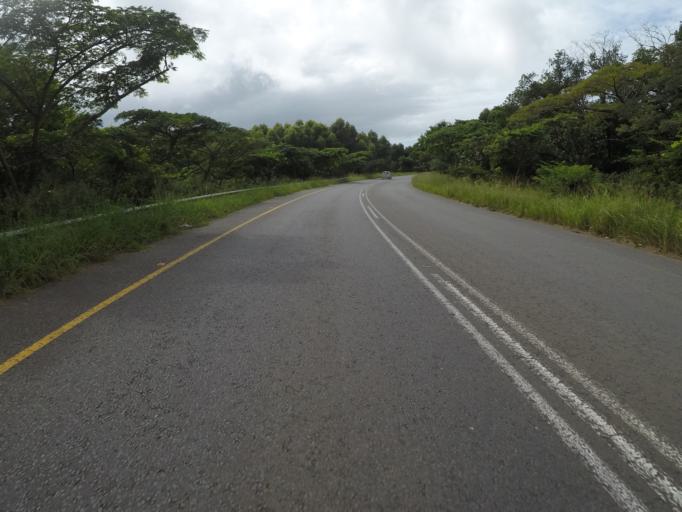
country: ZA
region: KwaZulu-Natal
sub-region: uThungulu District Municipality
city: eSikhawini
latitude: -28.8644
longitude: 31.8940
